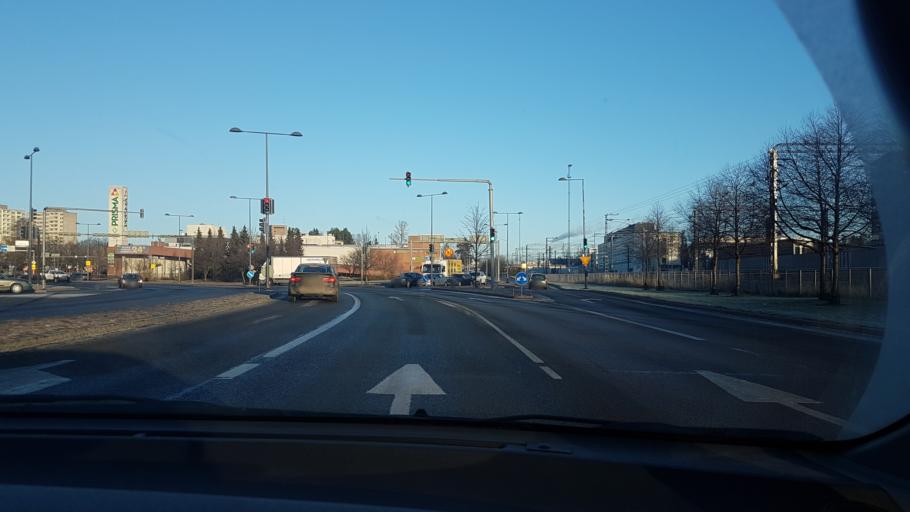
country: FI
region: Uusimaa
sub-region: Helsinki
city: Kerava
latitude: 60.3991
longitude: 25.1036
